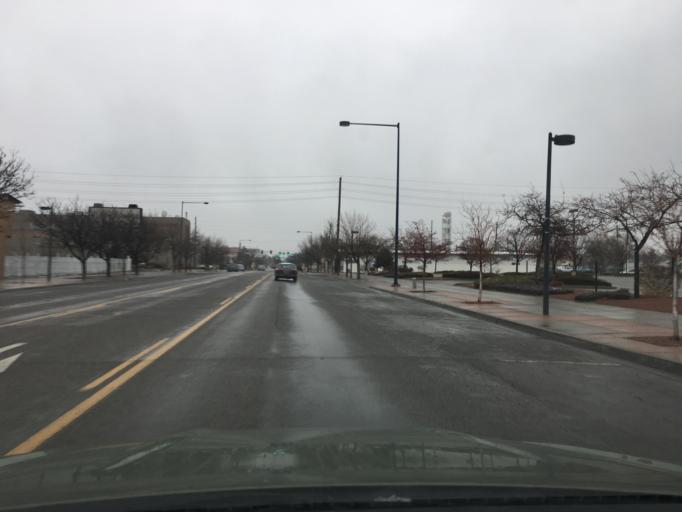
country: US
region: Colorado
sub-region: Mesa County
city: Grand Junction
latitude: 39.0625
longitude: -108.5610
